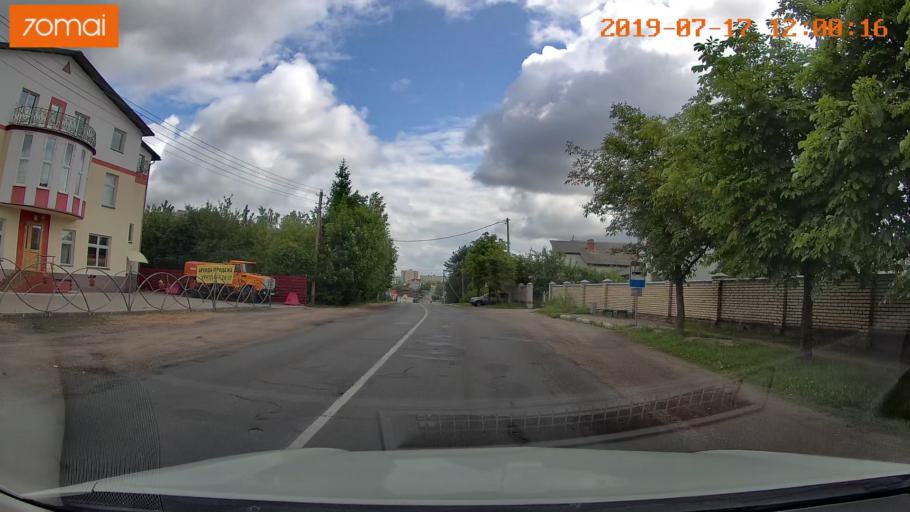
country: BY
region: Minsk
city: Borovlyany
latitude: 54.0038
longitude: 27.6631
